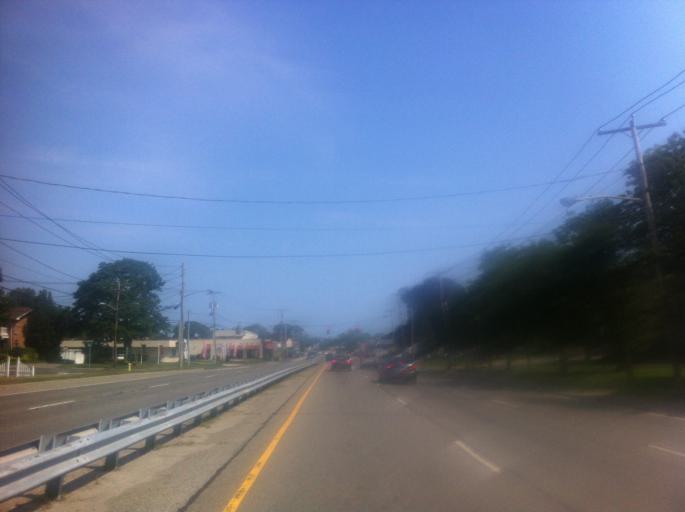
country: US
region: New York
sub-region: Suffolk County
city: West Babylon
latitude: 40.7043
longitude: -73.3449
